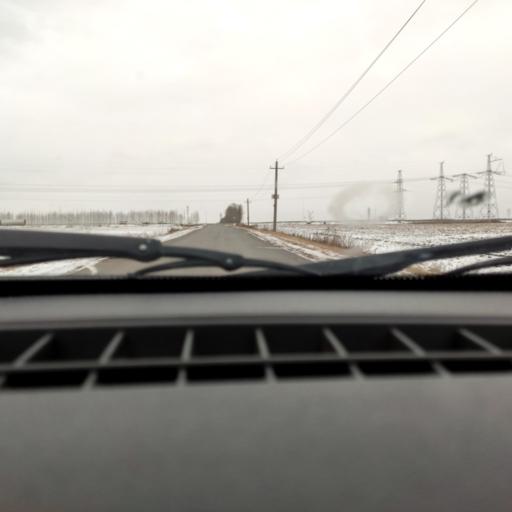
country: RU
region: Bashkortostan
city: Tolbazy
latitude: 54.2480
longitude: 55.8868
